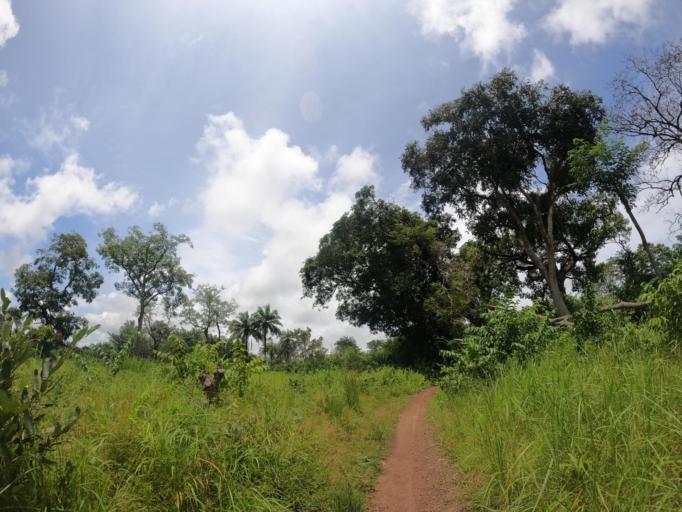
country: SL
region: Northern Province
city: Binkolo
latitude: 9.1462
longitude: -12.2447
